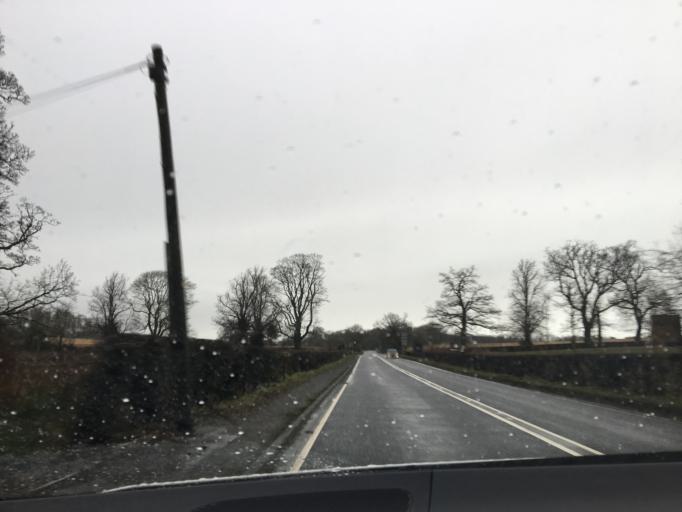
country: GB
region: Scotland
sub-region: Stirling
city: Doune
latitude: 56.1652
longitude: -4.0637
